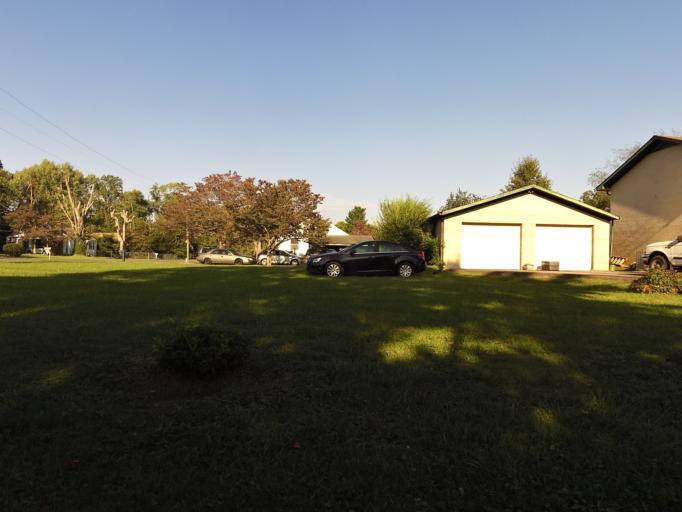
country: US
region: Tennessee
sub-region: Knox County
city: Knoxville
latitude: 36.0178
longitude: -83.9023
